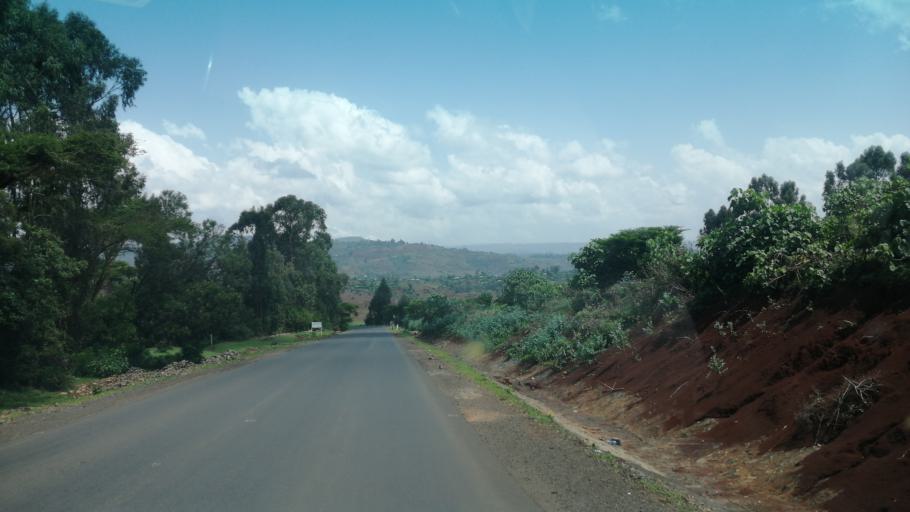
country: ET
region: Oromiya
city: Gedo
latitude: 8.9761
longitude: 37.5624
